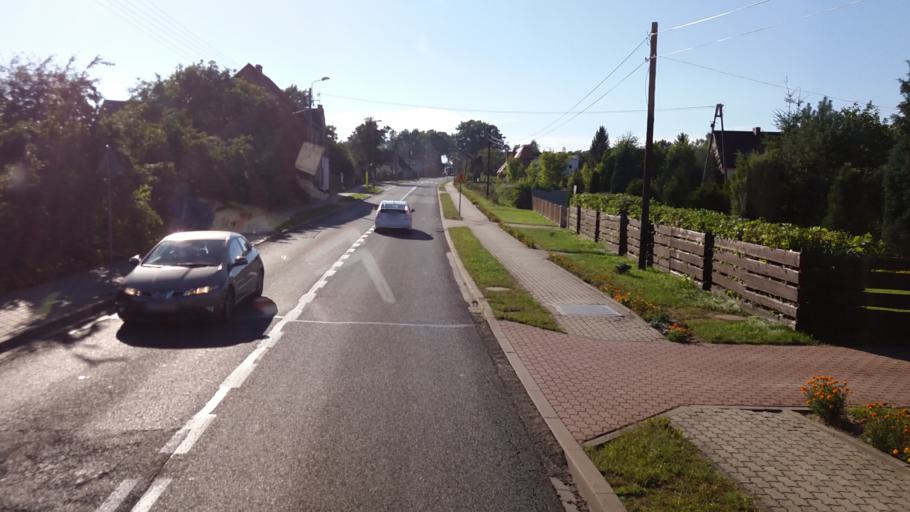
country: PL
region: West Pomeranian Voivodeship
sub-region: Powiat drawski
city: Kalisz Pomorski
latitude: 53.2957
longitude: 15.8459
